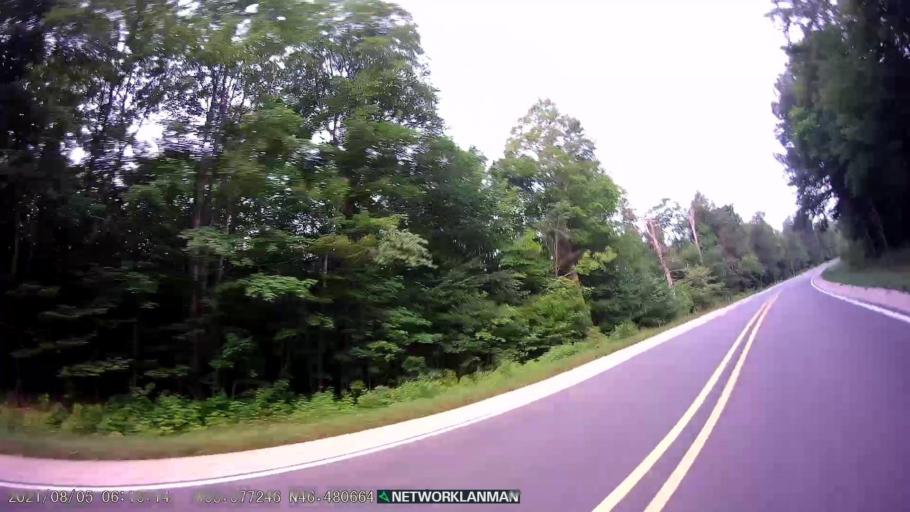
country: US
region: Michigan
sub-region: Luce County
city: Newberry
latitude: 46.4817
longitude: -85.0792
